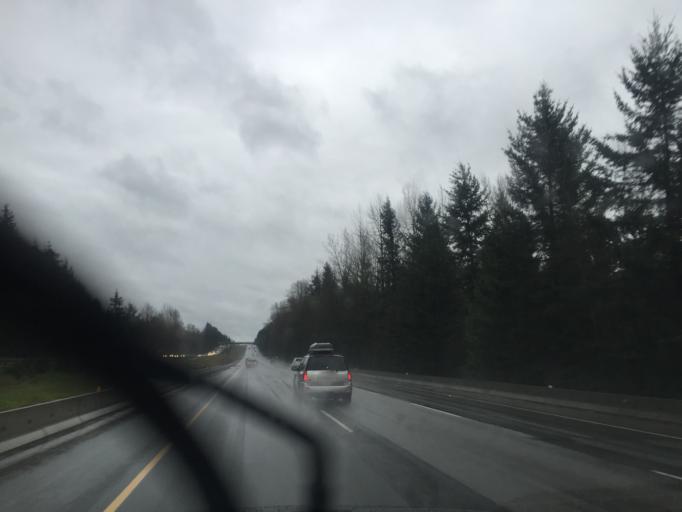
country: CA
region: British Columbia
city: Langley
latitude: 49.1233
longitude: -122.5484
